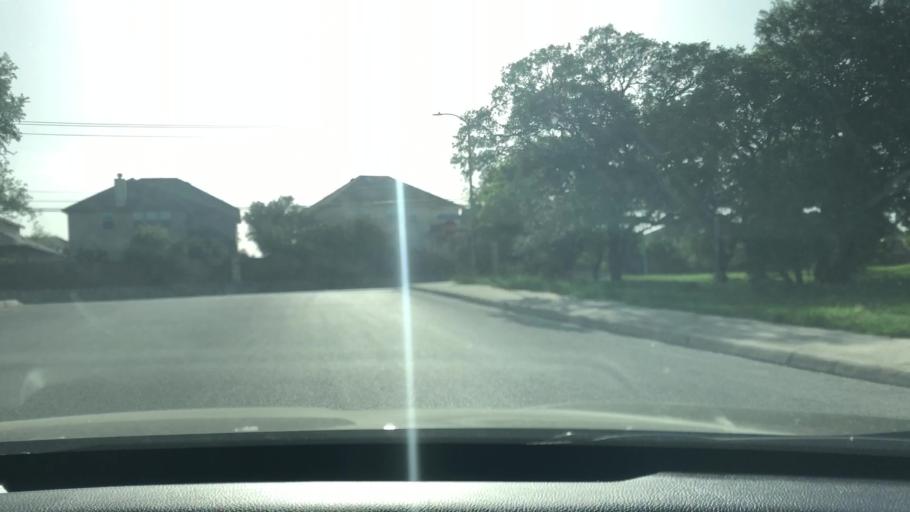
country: US
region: Texas
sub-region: Bexar County
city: Helotes
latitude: 29.5587
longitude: -98.6436
